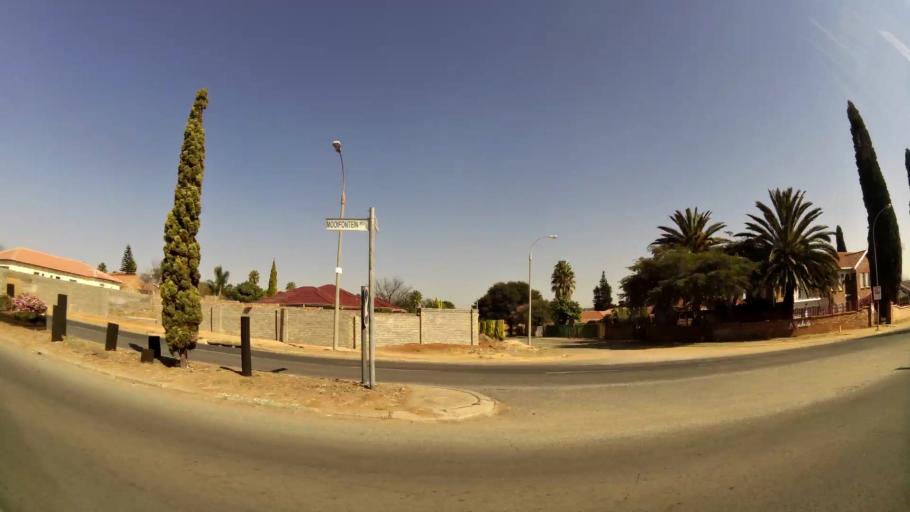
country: ZA
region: Gauteng
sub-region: Ekurhuleni Metropolitan Municipality
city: Tembisa
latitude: -26.0417
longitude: 28.2236
